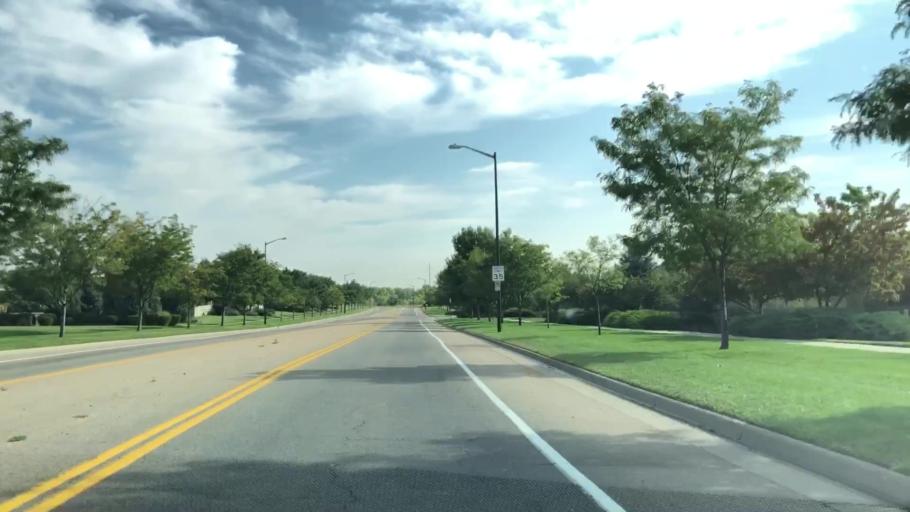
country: US
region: Colorado
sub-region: Larimer County
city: Loveland
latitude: 40.4236
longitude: -105.0510
